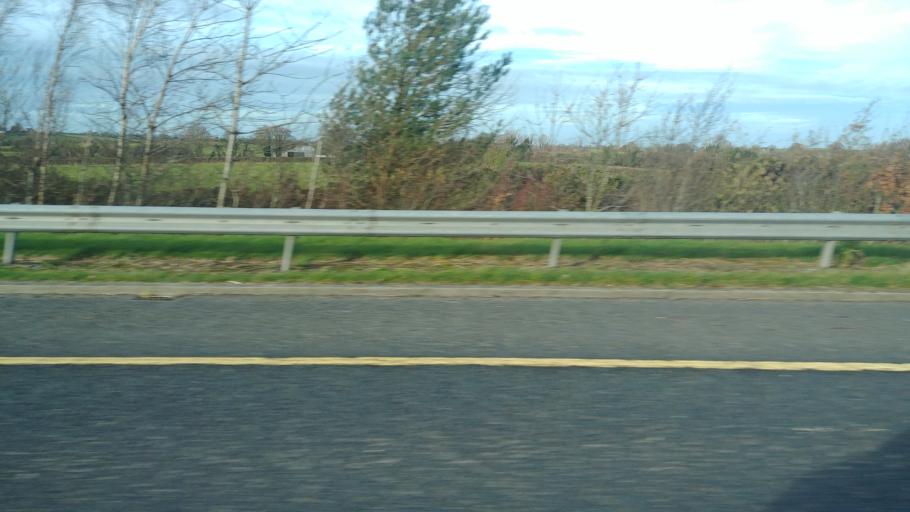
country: IE
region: Leinster
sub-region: Lu
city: Dromiskin
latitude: 53.9110
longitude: -6.4174
